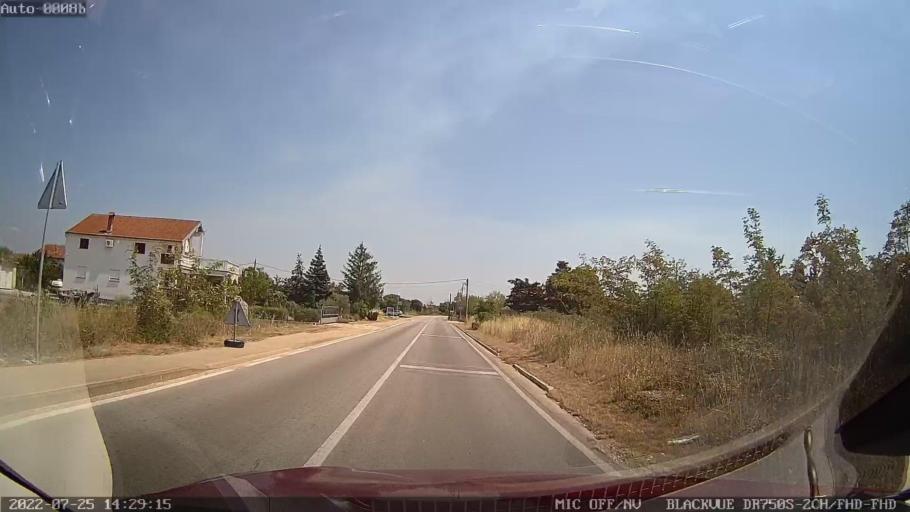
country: HR
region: Zadarska
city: Policnik
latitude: 44.1211
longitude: 15.3549
